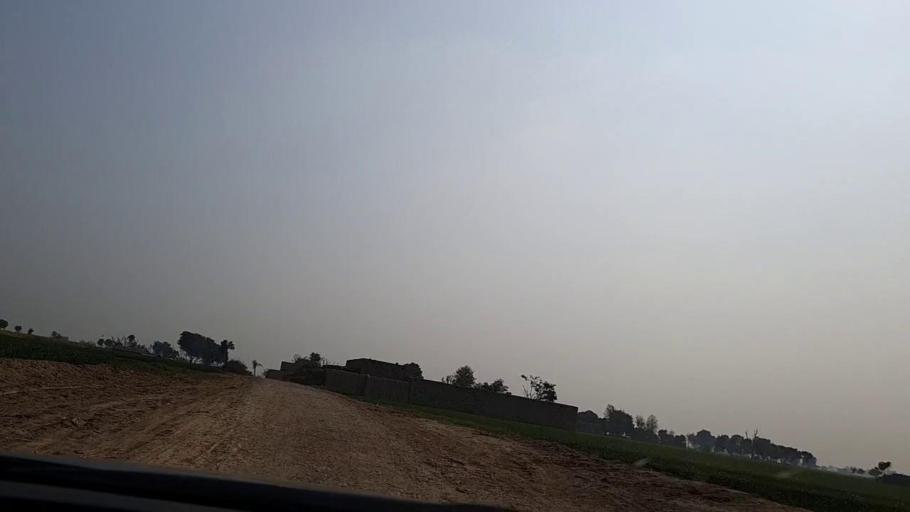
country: PK
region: Sindh
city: Sakrand
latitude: 26.1450
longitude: 68.2332
